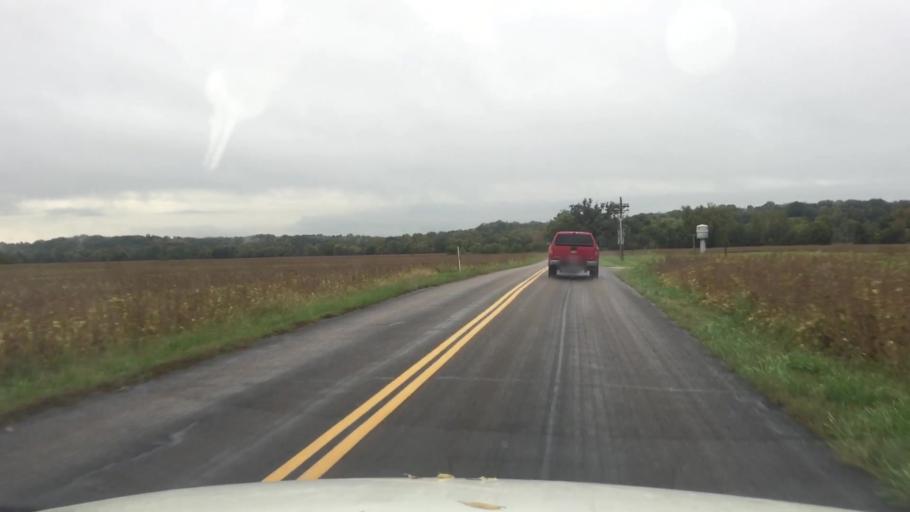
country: US
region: Missouri
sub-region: Boone County
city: Columbia
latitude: 38.8953
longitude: -92.4647
